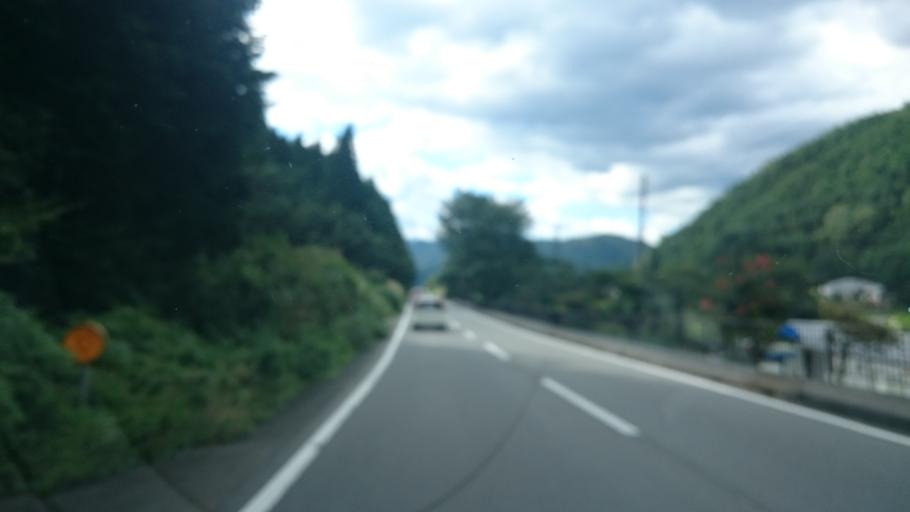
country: JP
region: Gifu
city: Gujo
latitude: 35.7591
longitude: 137.2984
